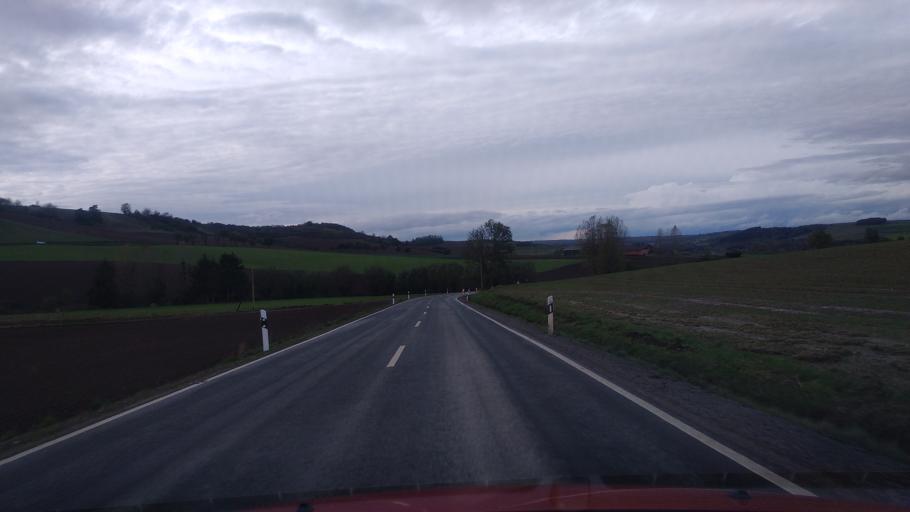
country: DE
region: North Rhine-Westphalia
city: Brakel
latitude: 51.6737
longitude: 9.2312
